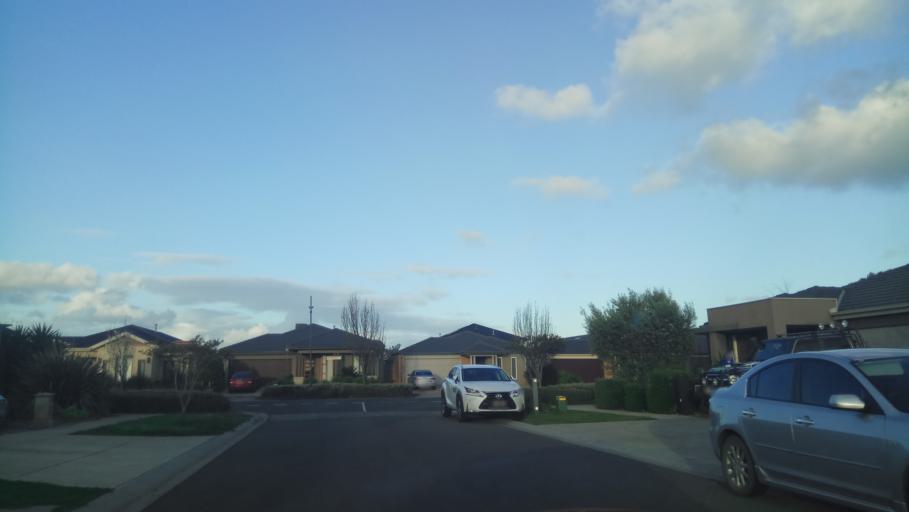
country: AU
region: Victoria
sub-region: Wyndham
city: Point Cook
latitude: -37.9119
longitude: 144.7763
